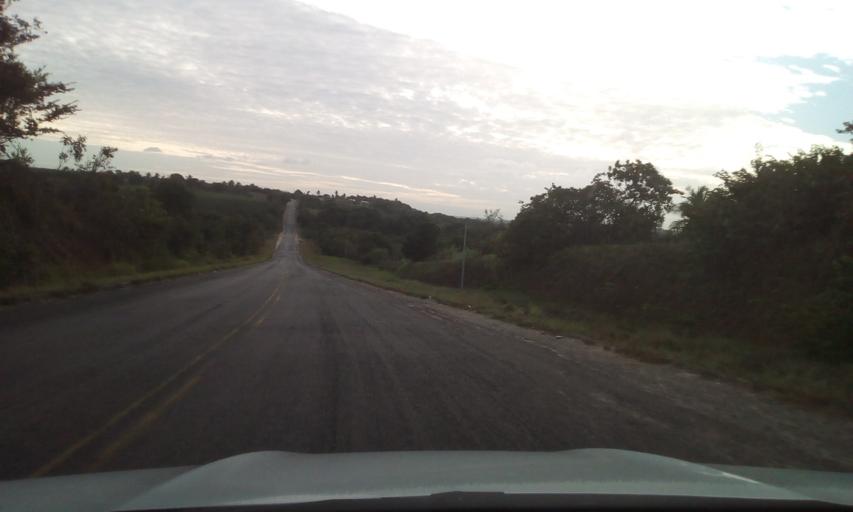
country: BR
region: Paraiba
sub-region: Conde
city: Conde
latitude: -7.2405
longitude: -34.8351
